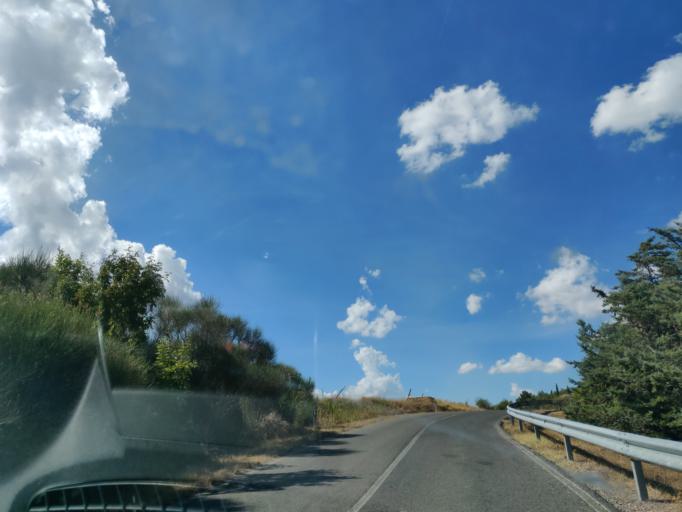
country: IT
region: Tuscany
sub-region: Provincia di Siena
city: Radicofani
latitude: 42.9463
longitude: 11.7345
